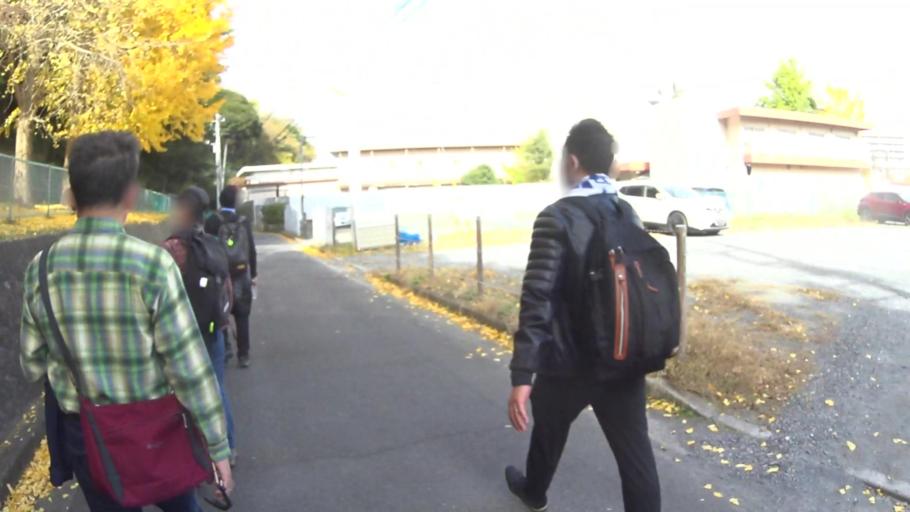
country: JP
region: Ibaraki
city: Mito-shi
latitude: 36.3738
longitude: 140.4842
